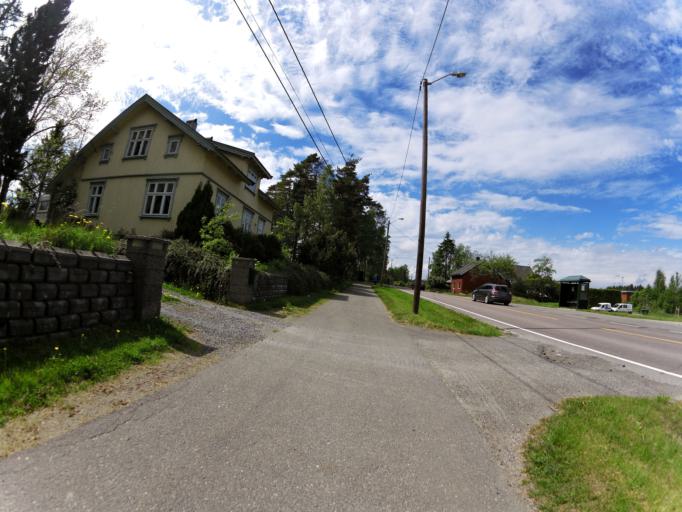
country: NO
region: Ostfold
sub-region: Rade
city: Karlshus
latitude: 59.3546
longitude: 10.8498
